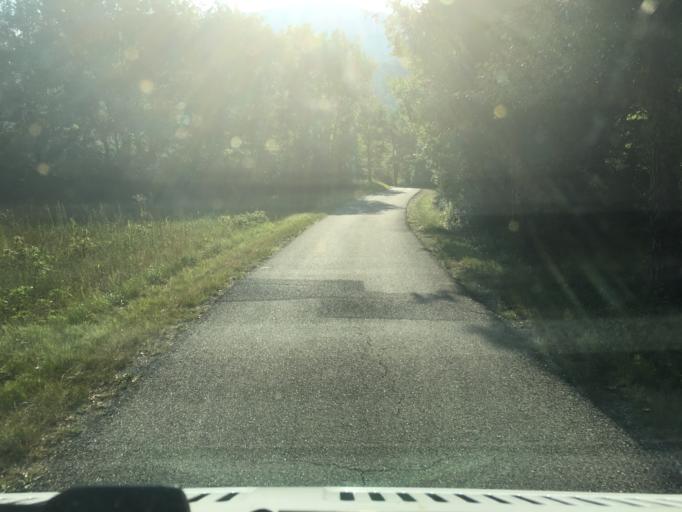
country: FR
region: Provence-Alpes-Cote d'Azur
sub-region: Departement des Alpes-de-Haute-Provence
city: Mallemoisson
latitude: 43.9393
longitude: 6.1957
